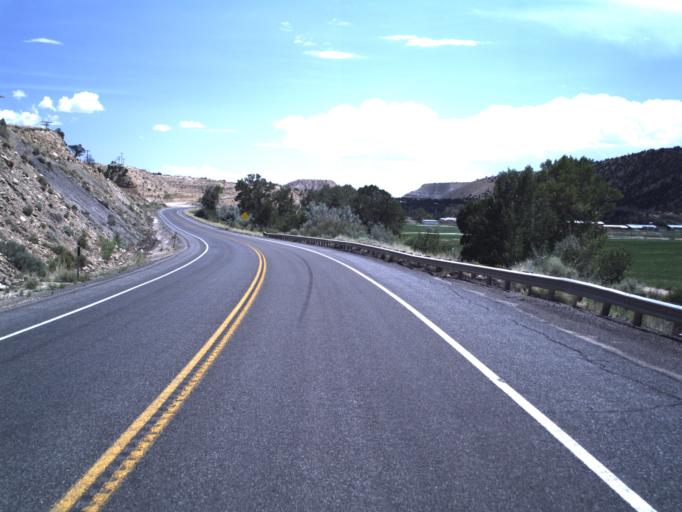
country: US
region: Utah
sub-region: Emery County
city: Huntington
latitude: 39.3767
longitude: -111.0686
